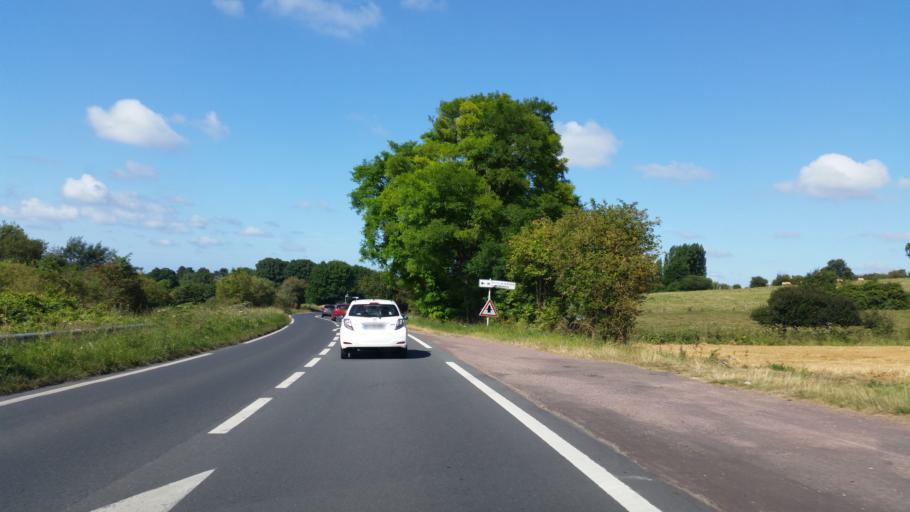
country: FR
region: Lower Normandy
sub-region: Departement du Calvados
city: Amfreville
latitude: 49.2589
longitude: -0.2372
